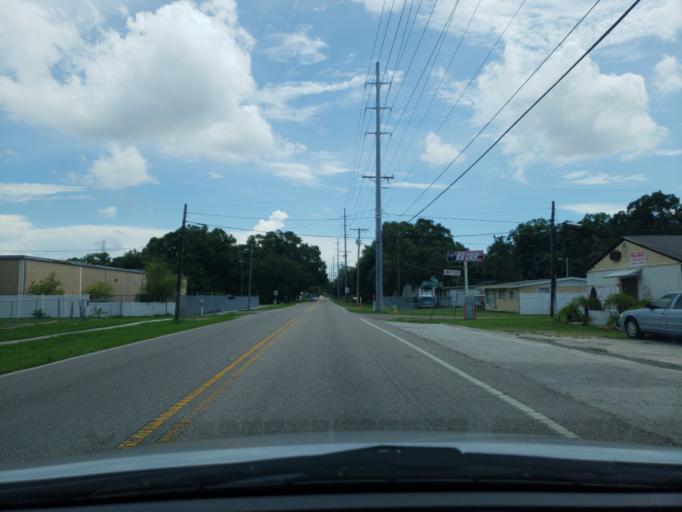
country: US
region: Florida
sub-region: Hillsborough County
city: East Lake-Orient Park
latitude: 27.9751
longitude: -82.3731
